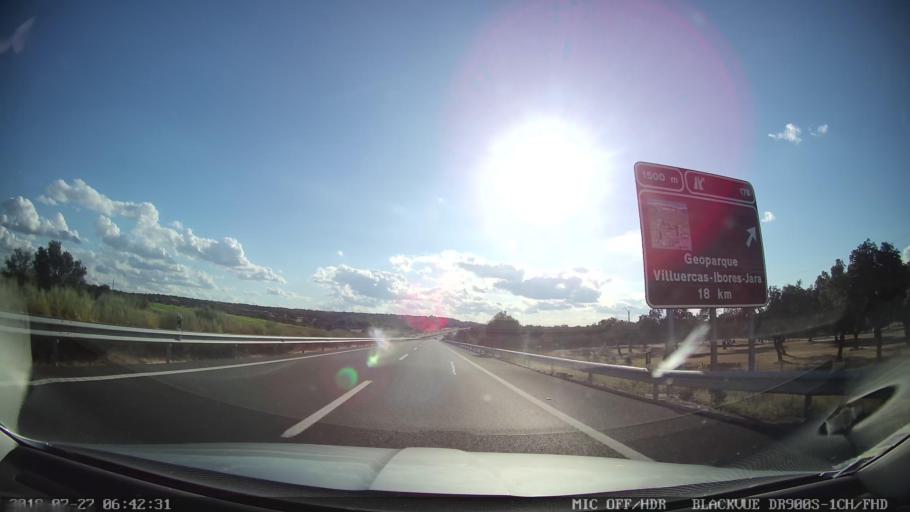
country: ES
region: Extremadura
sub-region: Provincia de Caceres
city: Peraleda de la Mata
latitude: 39.8894
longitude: -5.4870
